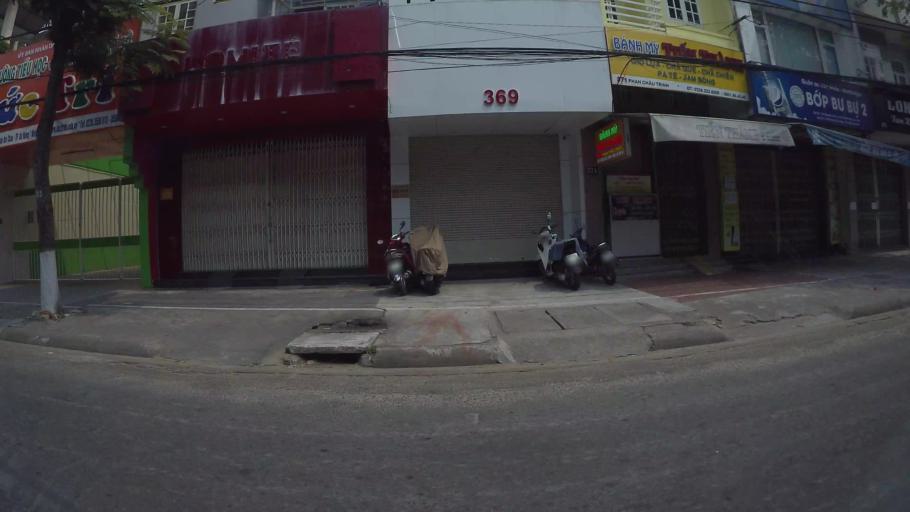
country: VN
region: Da Nang
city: Da Nang
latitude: 16.0566
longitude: 108.2189
